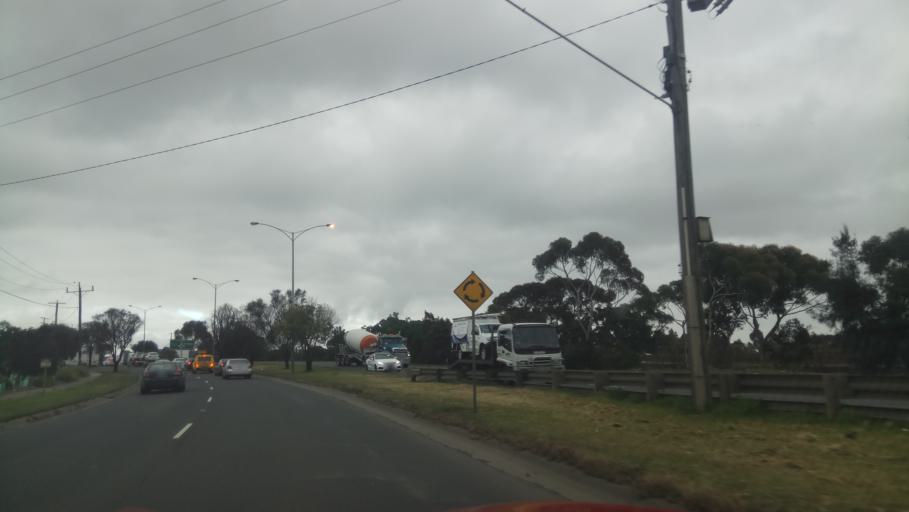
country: AU
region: Victoria
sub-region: Brimbank
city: Brooklyn
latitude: -37.8294
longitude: 144.8276
